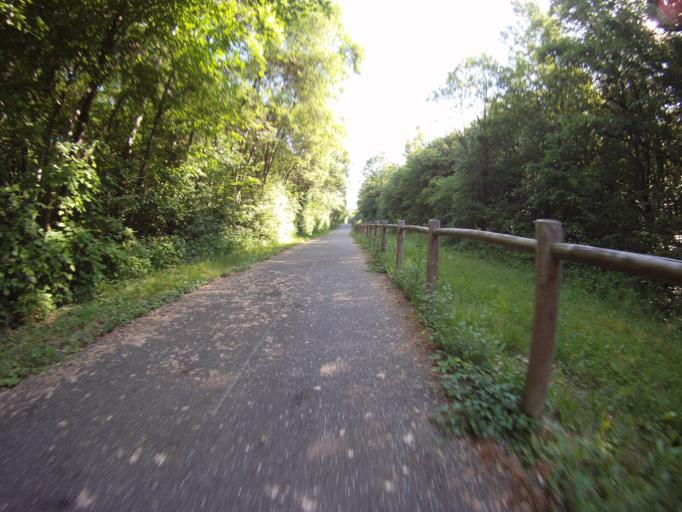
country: FR
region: Lorraine
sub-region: Departement de Meurthe-et-Moselle
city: Champenoux
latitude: 48.7438
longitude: 6.3187
